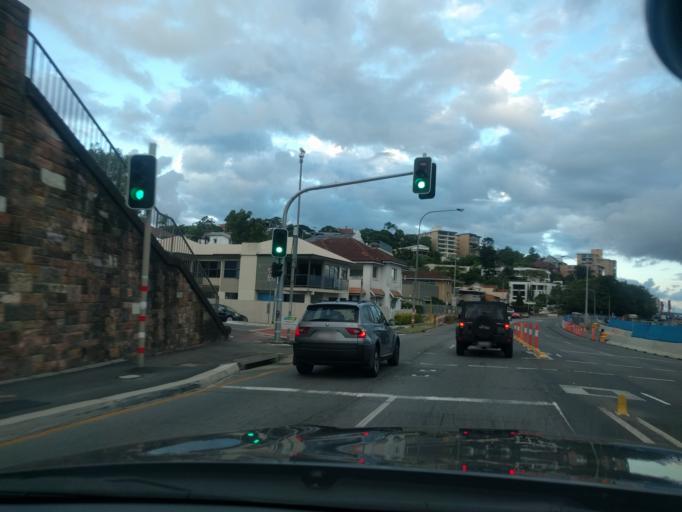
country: AU
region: Queensland
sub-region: Brisbane
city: Ascot
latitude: -27.4392
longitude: 153.0551
